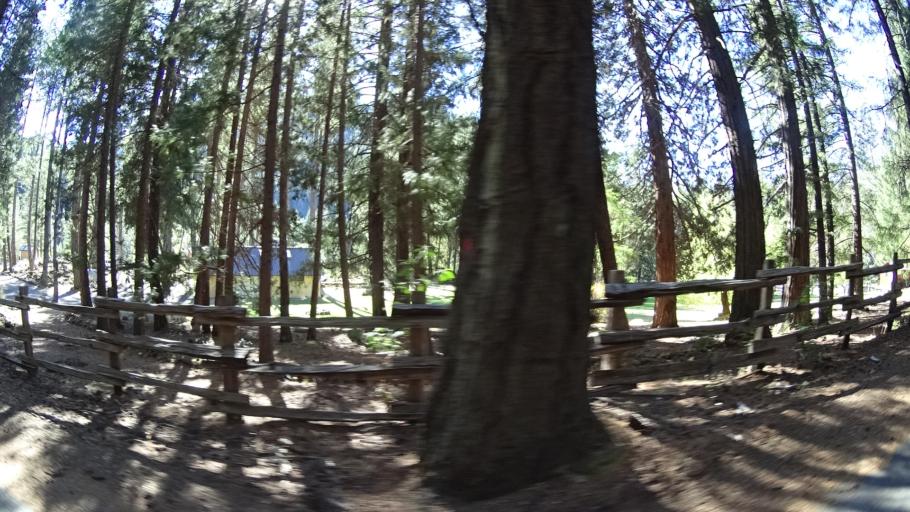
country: US
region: California
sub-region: Siskiyou County
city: Happy Camp
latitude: 41.2974
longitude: -123.1185
